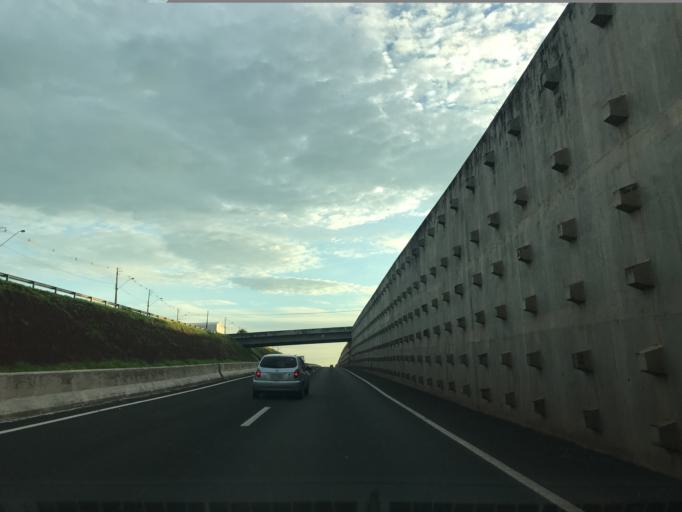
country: BR
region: Parana
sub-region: Maringa
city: Maringa
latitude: -23.3776
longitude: -51.9430
